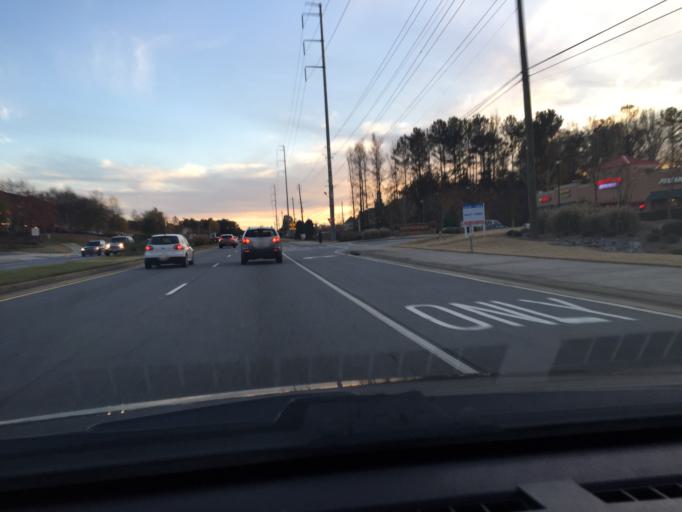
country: US
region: Georgia
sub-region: Fulton County
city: Johns Creek
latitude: 34.0363
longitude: -84.1855
